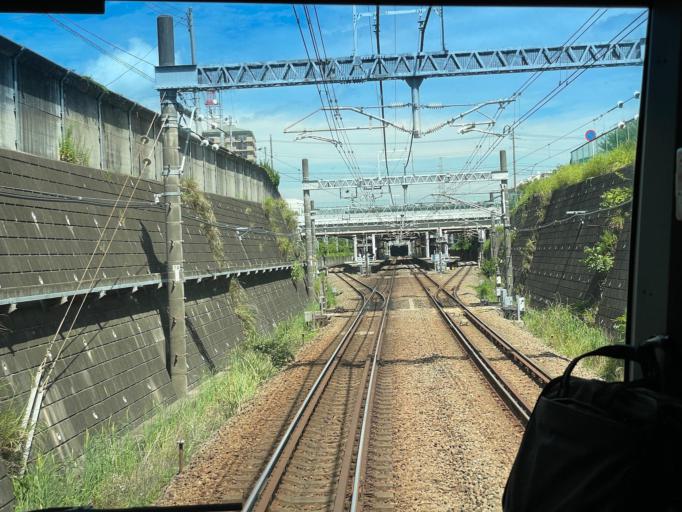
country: JP
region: Kanagawa
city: Minami-rinkan
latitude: 35.4298
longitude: 139.4927
